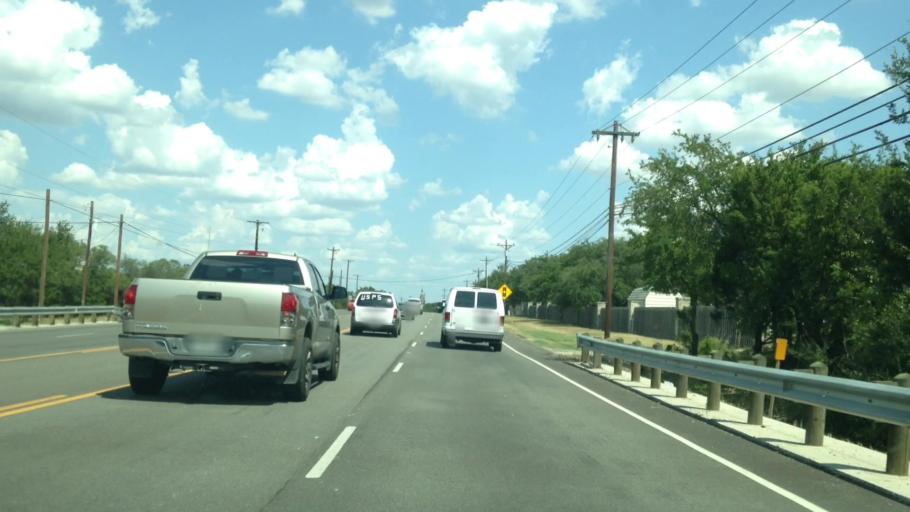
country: US
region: Texas
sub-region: Williamson County
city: Georgetown
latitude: 30.6332
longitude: -97.7162
